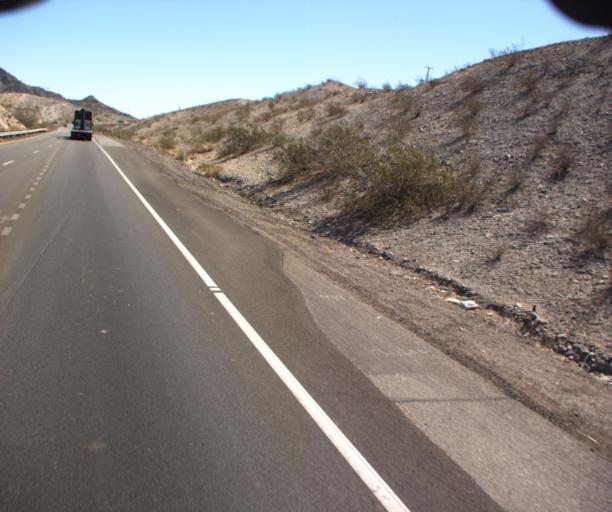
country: US
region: Arizona
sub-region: Yuma County
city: Fortuna Foothills
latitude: 32.6599
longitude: -114.3591
